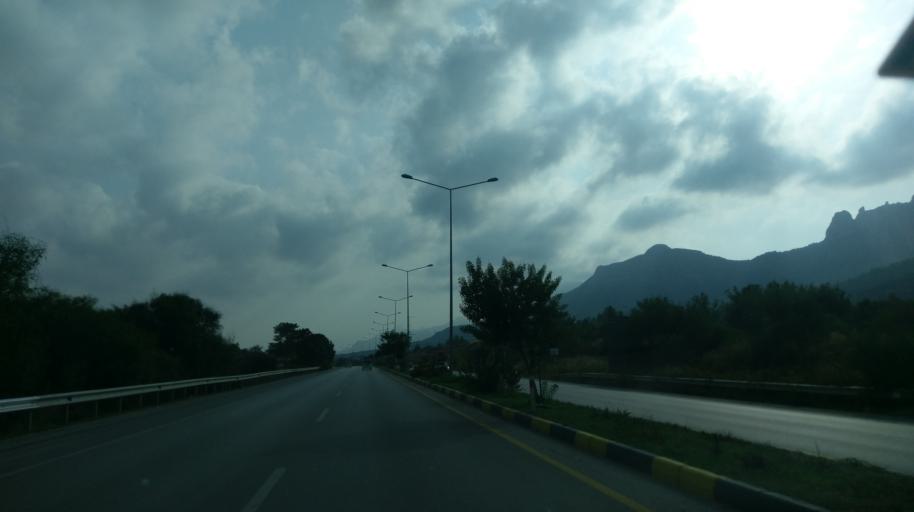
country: CY
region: Keryneia
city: Kyrenia
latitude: 35.3302
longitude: 33.2784
